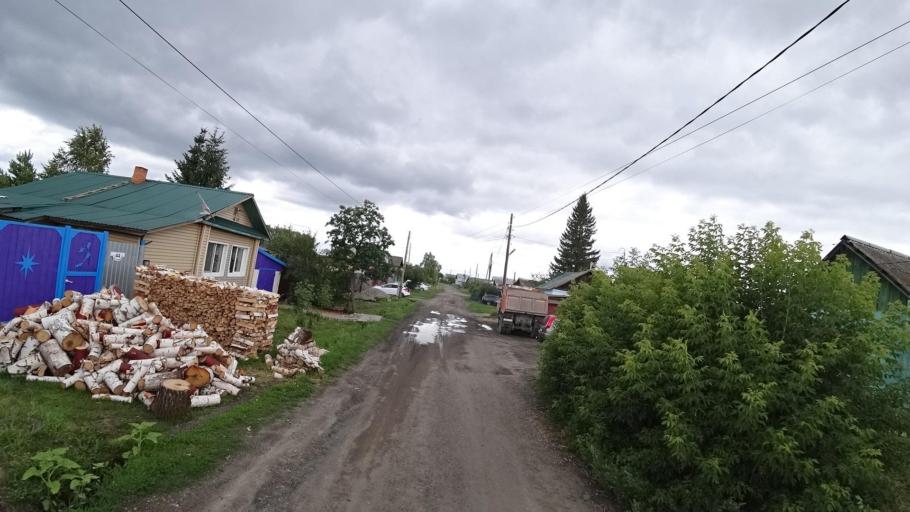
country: RU
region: Sverdlovsk
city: Kamyshlov
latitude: 56.8524
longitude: 62.6937
